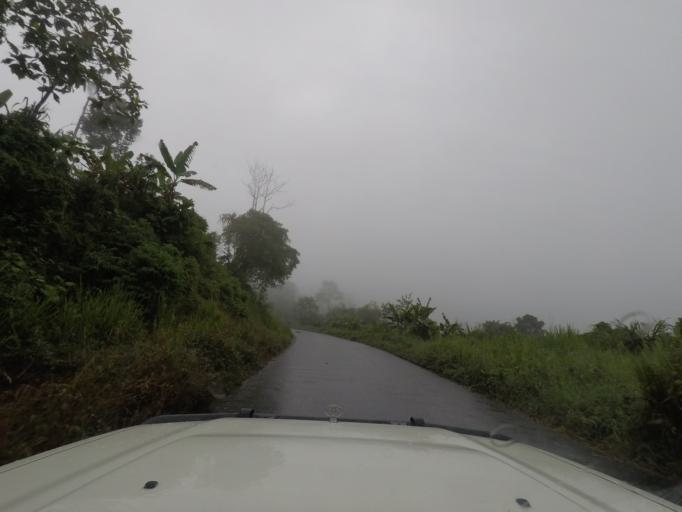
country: PG
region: Madang
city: Madang
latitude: -5.4495
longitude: 145.5102
